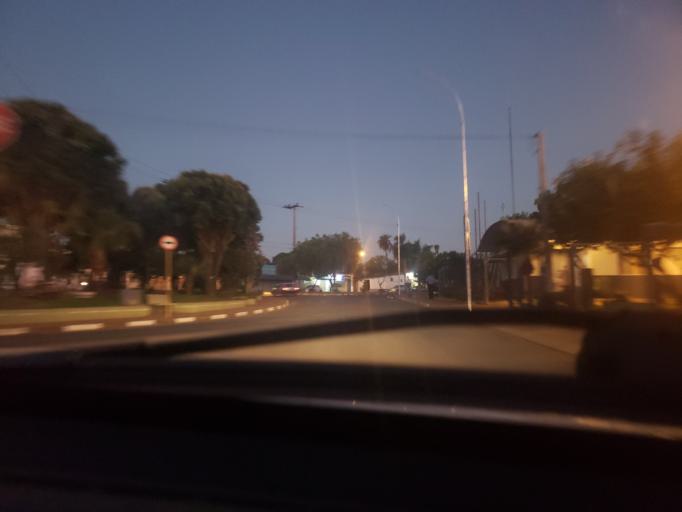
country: BR
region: Sao Paulo
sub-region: Conchal
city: Conchal
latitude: -22.2892
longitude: -47.1340
